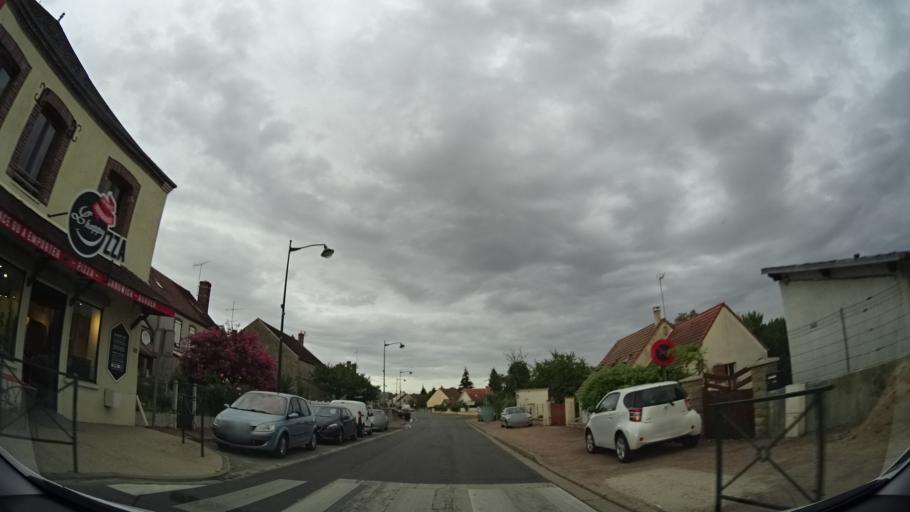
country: FR
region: Centre
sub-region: Departement du Loiret
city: Saint-Germain-des-Pres
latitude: 47.9531
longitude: 2.8415
